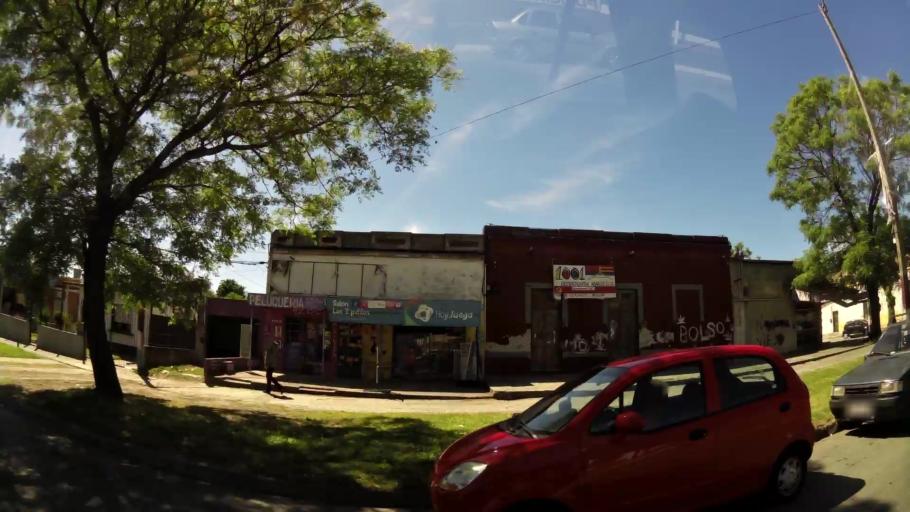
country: UY
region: Canelones
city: Paso de Carrasco
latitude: -34.8519
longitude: -56.1289
